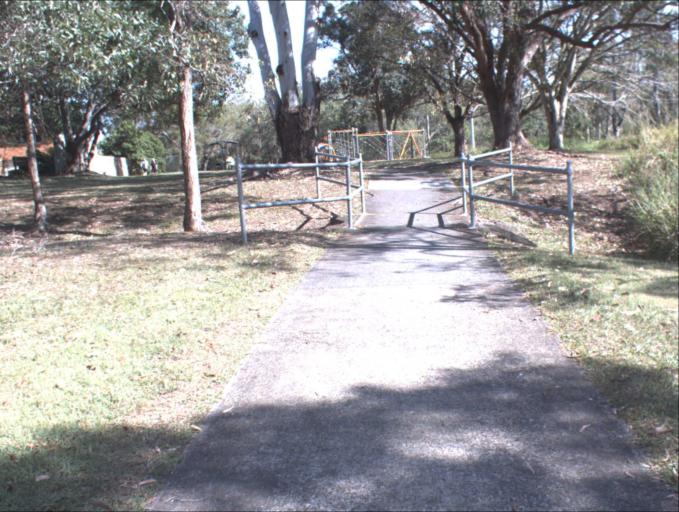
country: AU
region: Queensland
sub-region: Logan
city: Logan City
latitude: -27.6364
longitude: 153.1294
